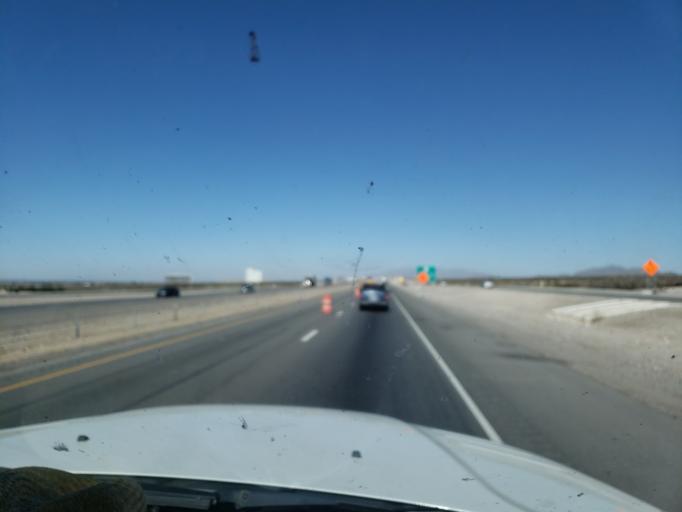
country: US
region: Texas
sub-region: El Paso County
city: Westway
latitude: 31.9342
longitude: -106.5827
